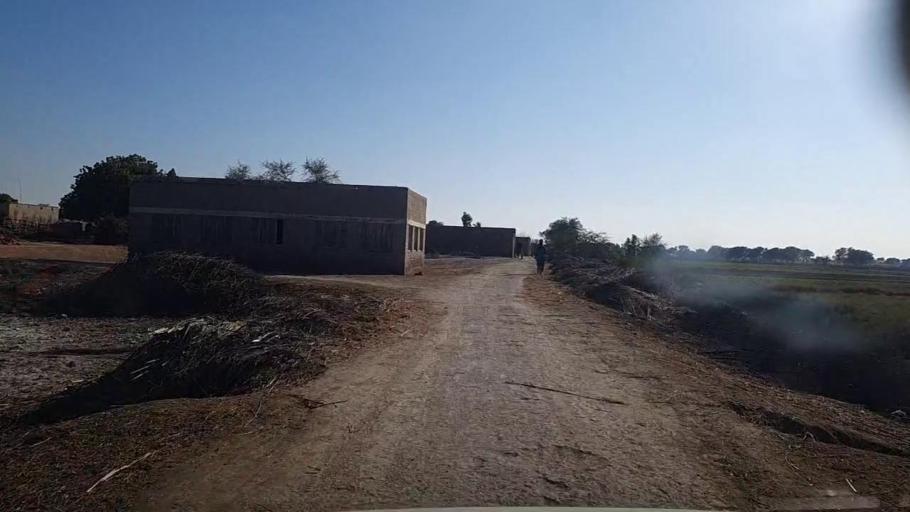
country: PK
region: Sindh
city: Khairpur
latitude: 27.9808
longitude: 69.7684
